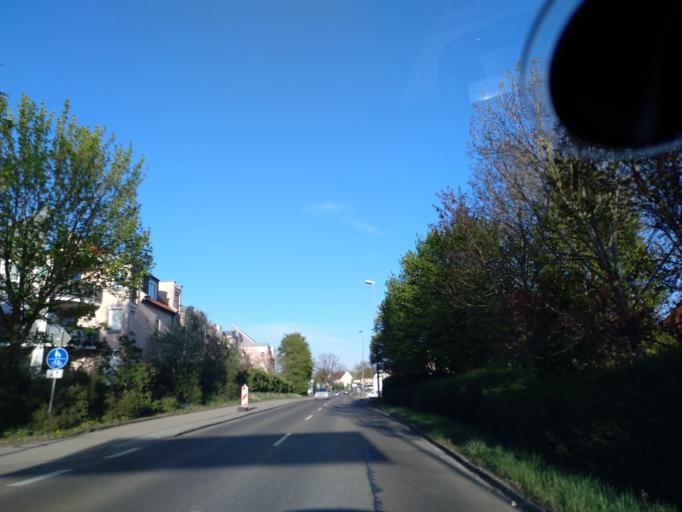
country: DE
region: Baden-Wuerttemberg
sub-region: Regierungsbezirk Stuttgart
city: Crailsheim
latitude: 49.1388
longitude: 10.0195
